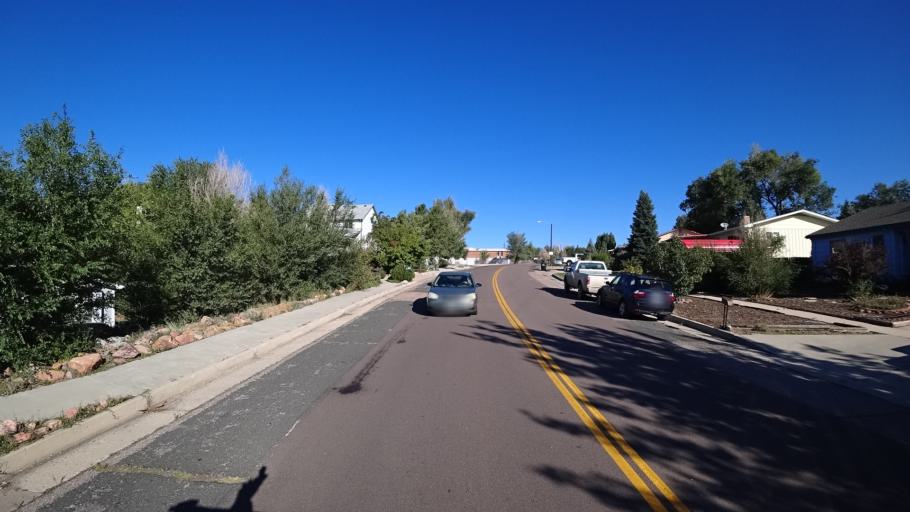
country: US
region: Colorado
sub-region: El Paso County
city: Colorado Springs
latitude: 38.8408
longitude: -104.8389
